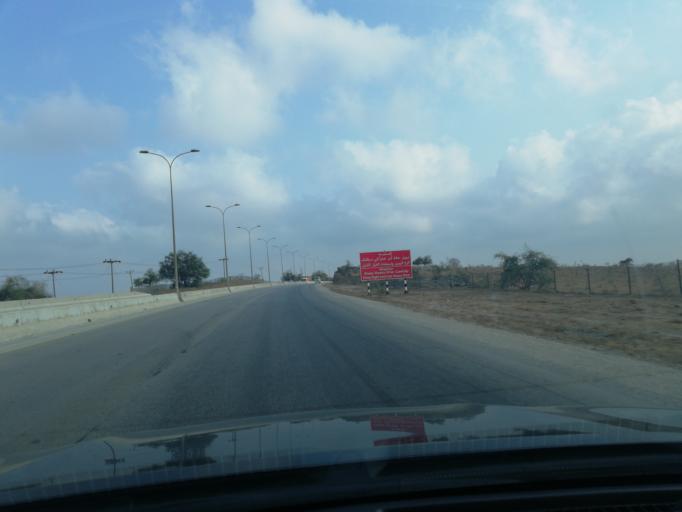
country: OM
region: Zufar
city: Salalah
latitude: 17.1783
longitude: 54.1218
